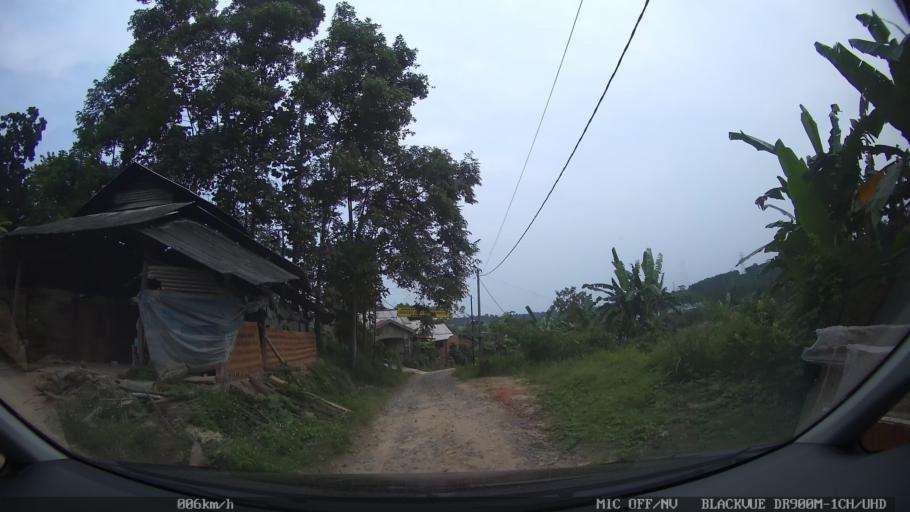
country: ID
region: Lampung
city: Panjang
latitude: -5.4280
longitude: 105.3392
